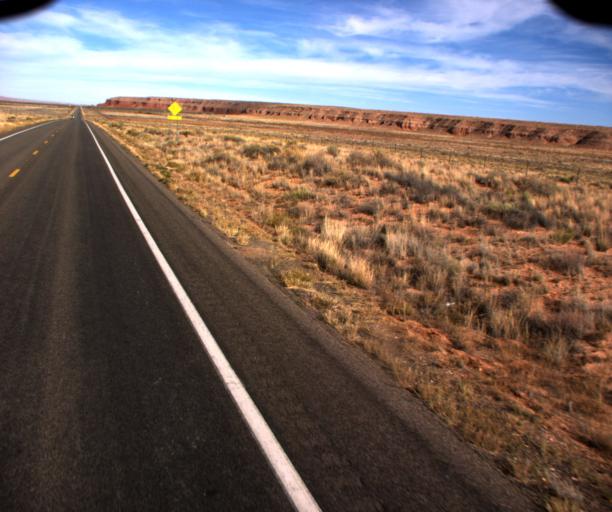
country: US
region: Arizona
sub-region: Navajo County
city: Kayenta
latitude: 36.7487
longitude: -110.0656
